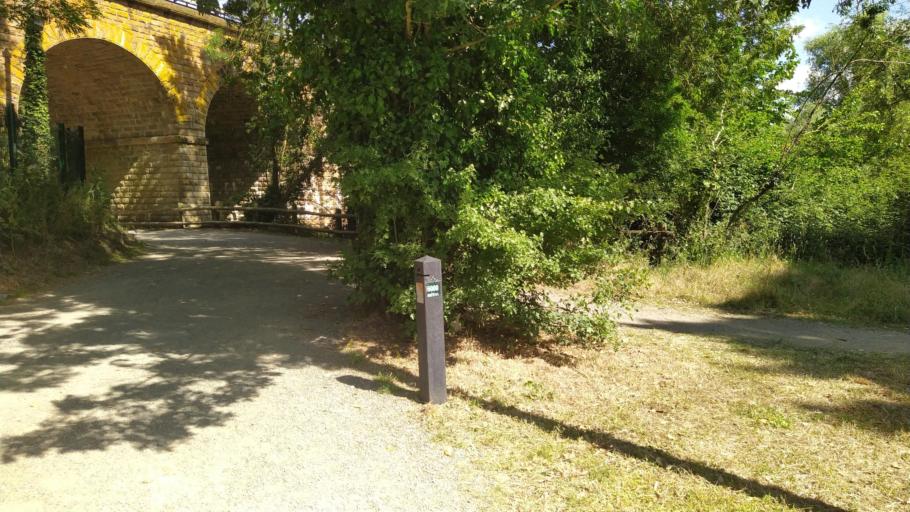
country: FR
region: Pays de la Loire
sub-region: Departement de la Loire-Atlantique
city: Saint-Sebastien-sur-Loire
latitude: 47.2093
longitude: -1.5136
